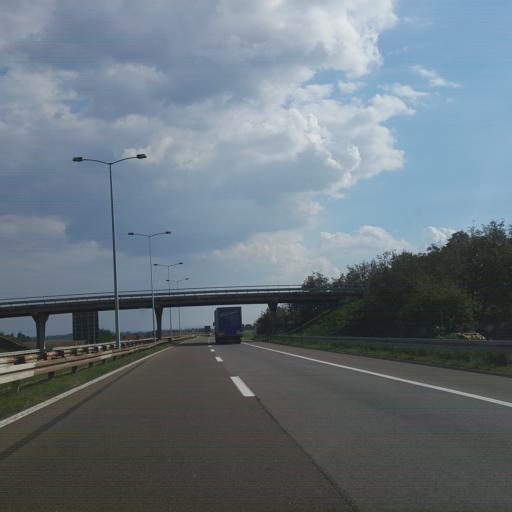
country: RS
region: Central Serbia
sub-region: Podunavski Okrug
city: Velika Plana
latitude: 44.3363
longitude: 21.0856
